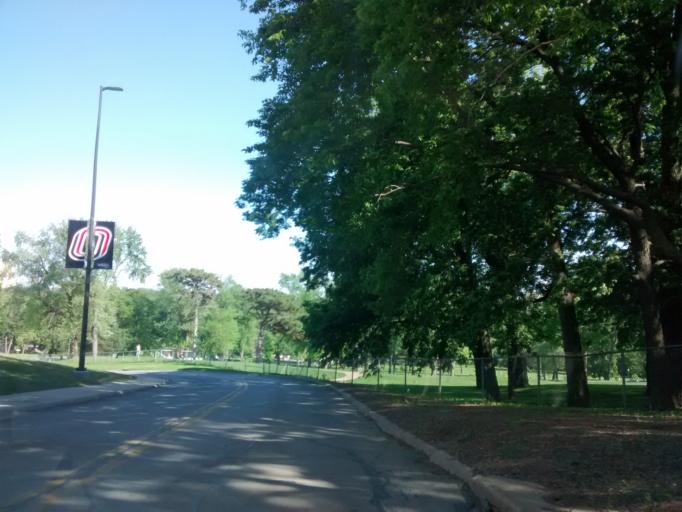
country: US
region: Nebraska
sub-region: Douglas County
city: Ralston
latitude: 41.2561
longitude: -96.0094
